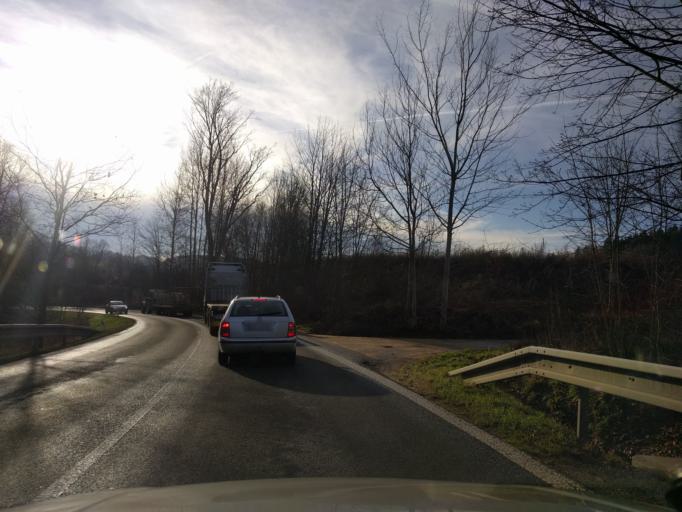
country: CZ
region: Liberecky
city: Mnisek
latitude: 50.8415
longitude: 15.0361
